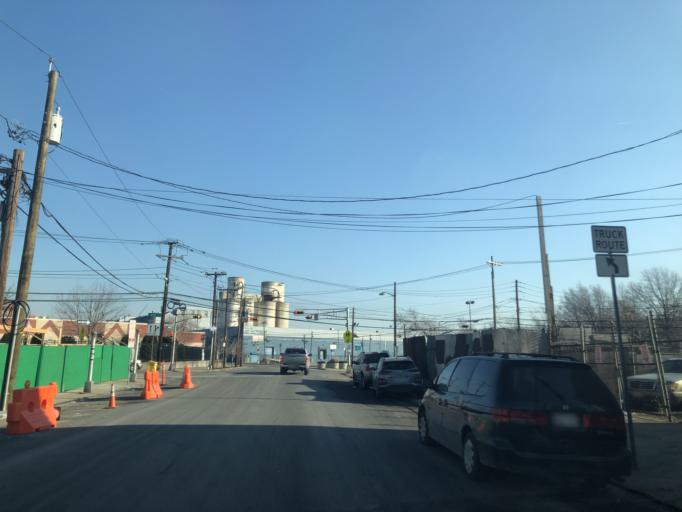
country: US
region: New Jersey
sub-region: Hudson County
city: Harrison
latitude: 40.7301
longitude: -74.1473
